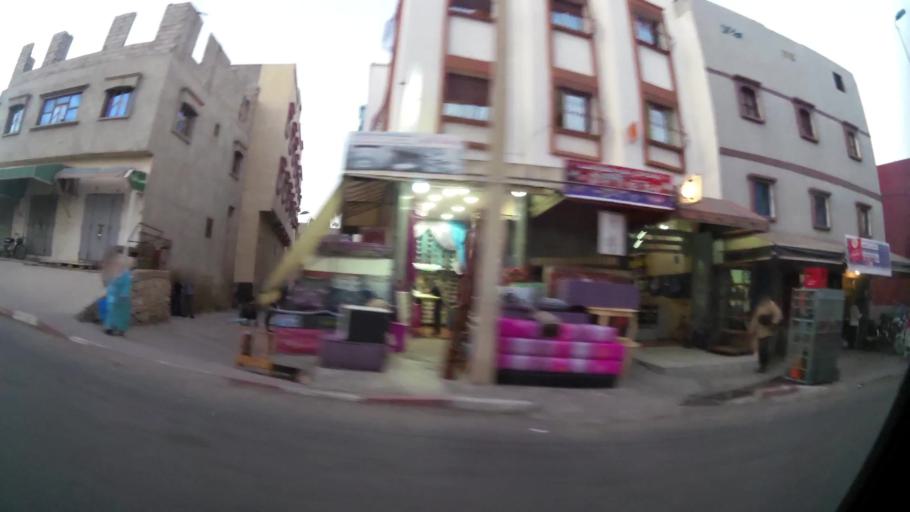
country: MA
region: Souss-Massa-Draa
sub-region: Inezgane-Ait Mellou
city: Inezgane
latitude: 30.3759
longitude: -9.4948
